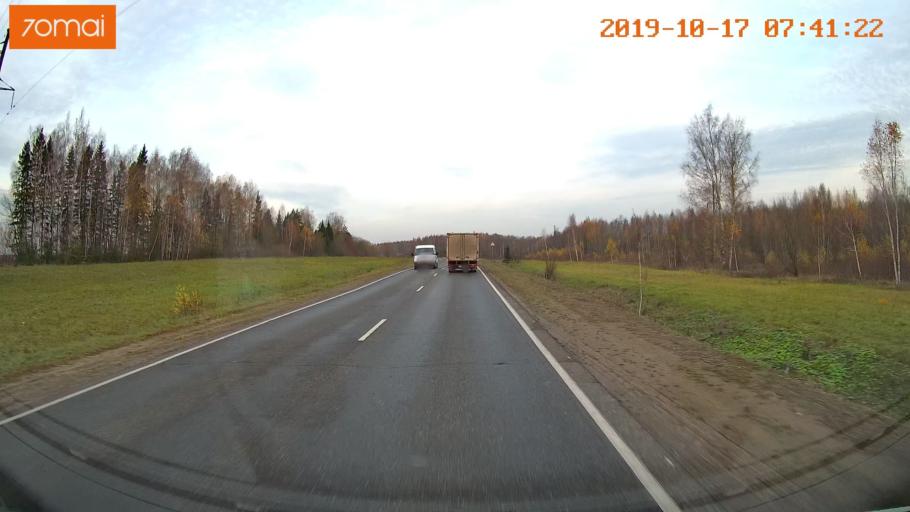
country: RU
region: Vladimir
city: Yur'yev-Pol'skiy
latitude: 56.4814
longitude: 39.8117
